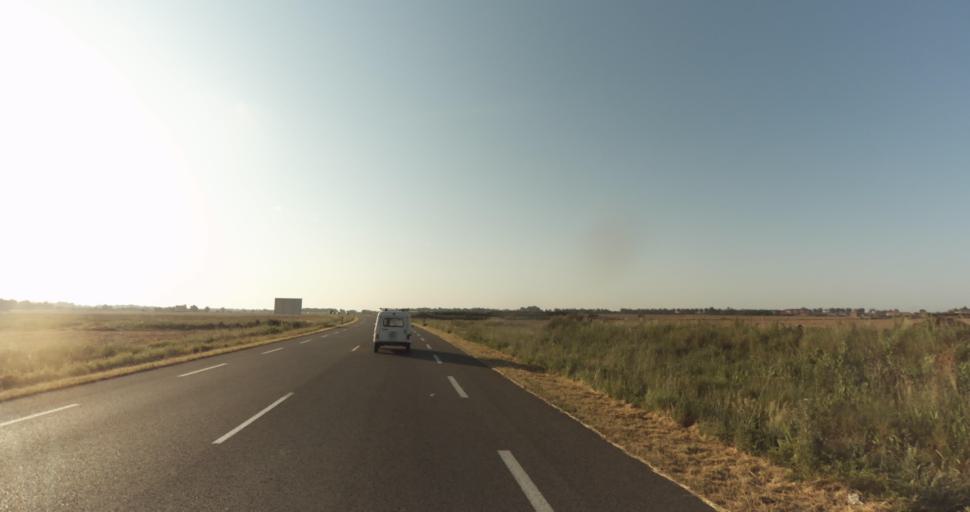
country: FR
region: Midi-Pyrenees
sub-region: Departement de la Haute-Garonne
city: Fontenilles
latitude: 43.5309
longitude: 1.1870
